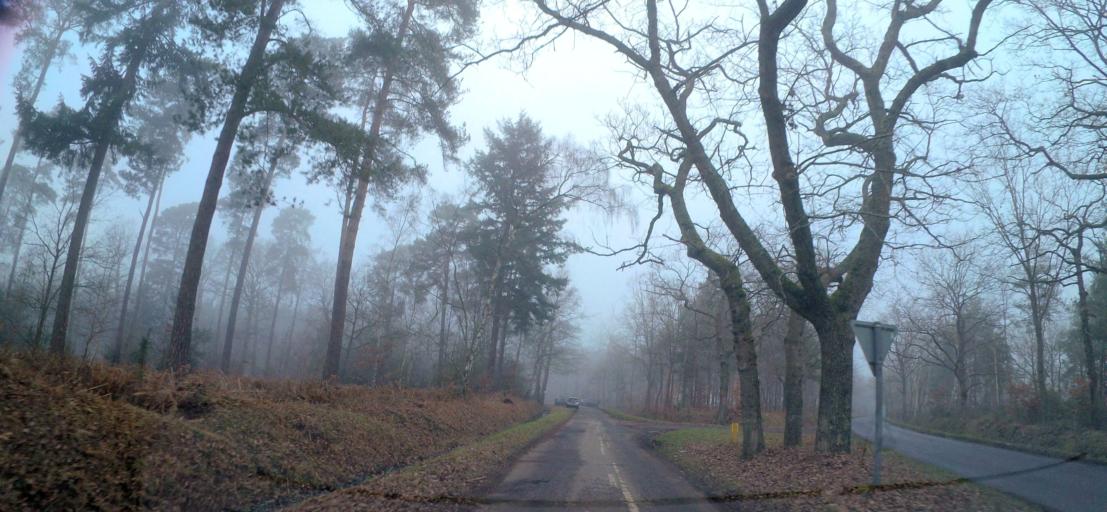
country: GB
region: England
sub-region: West Berkshire
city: Theale
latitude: 51.3936
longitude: -1.0888
